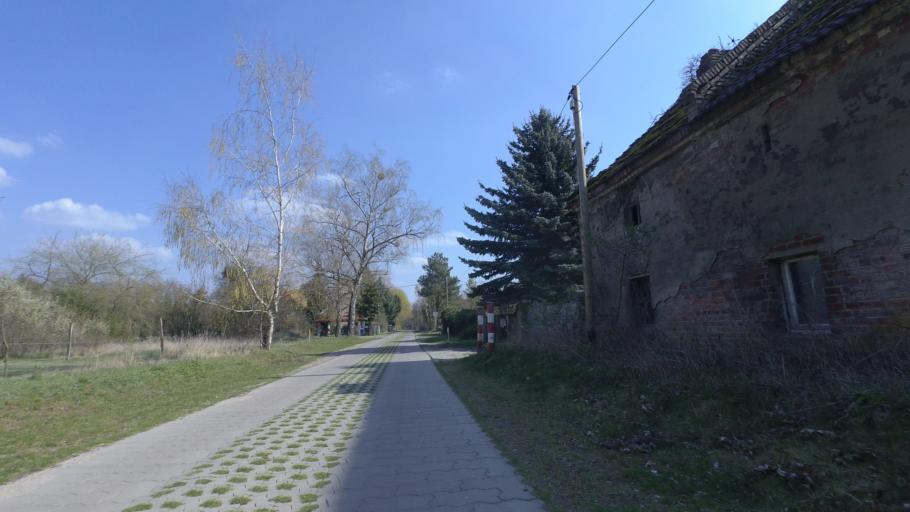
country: DE
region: Brandenburg
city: Teupitz
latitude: 52.1781
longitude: 13.5644
